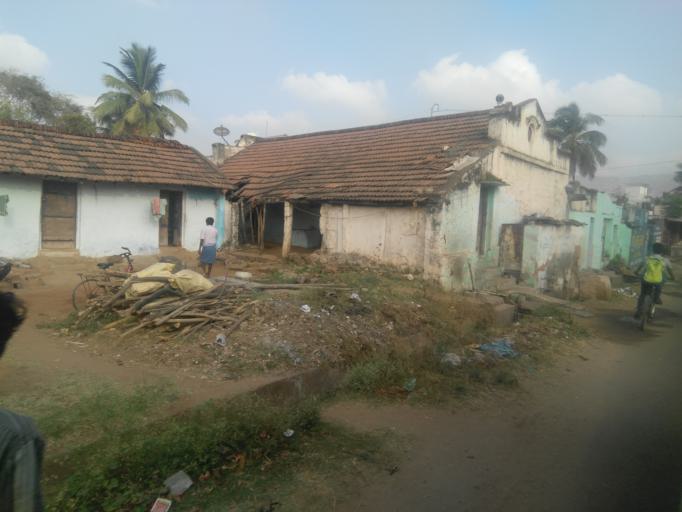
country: IN
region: Tamil Nadu
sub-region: Coimbatore
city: Perur
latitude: 11.0363
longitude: 76.8911
